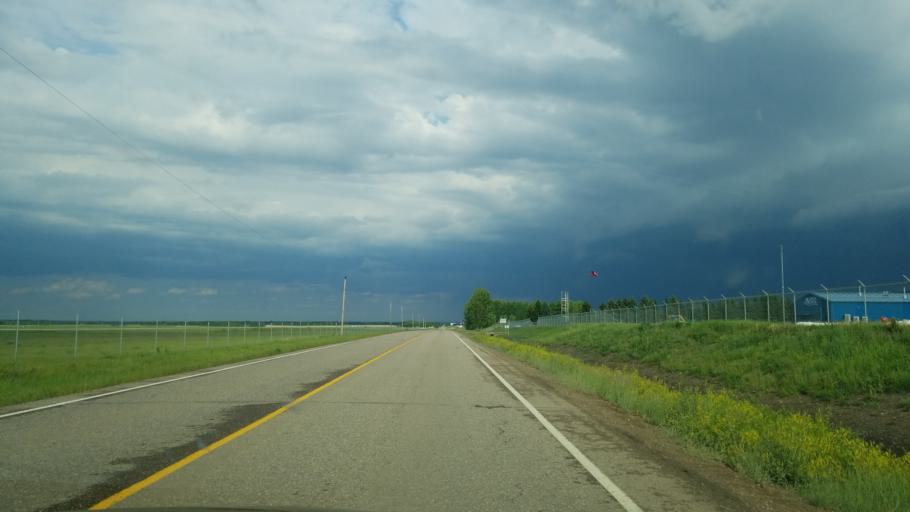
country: CA
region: Saskatchewan
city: Lloydminster
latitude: 53.3071
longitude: -110.0770
